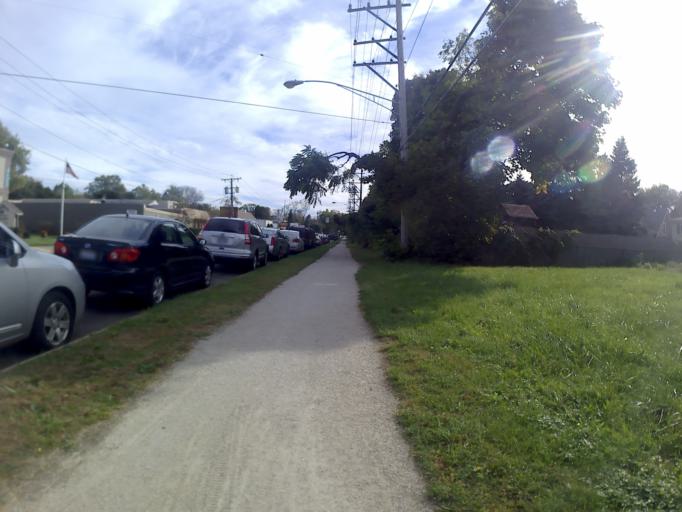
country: US
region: Illinois
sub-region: DuPage County
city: Wheaton
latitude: 41.8612
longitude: -88.1163
